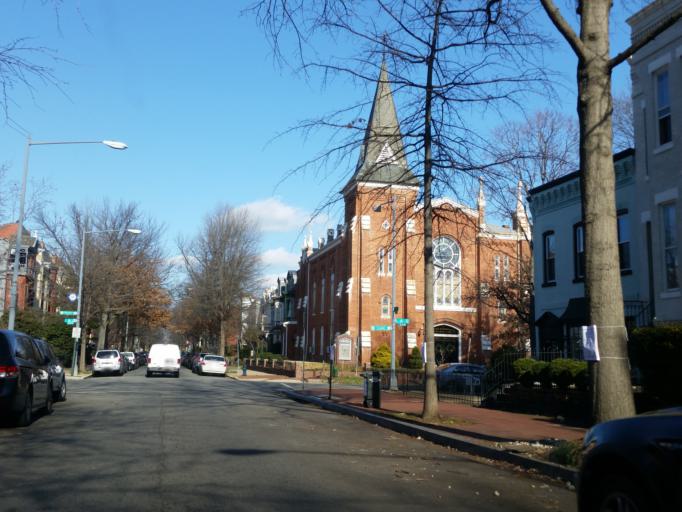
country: US
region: Washington, D.C.
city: Washington, D.C.
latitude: 38.8906
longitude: -77.0021
